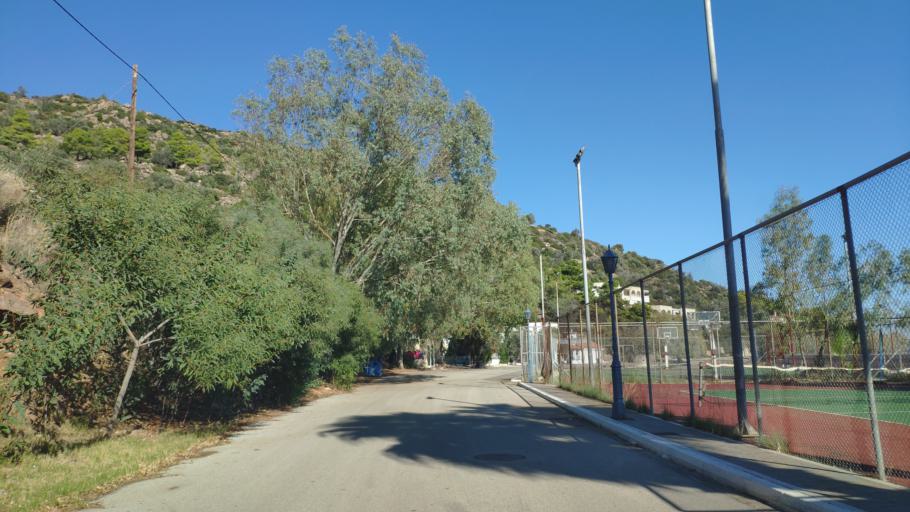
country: GR
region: Attica
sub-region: Nomos Piraios
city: Poros
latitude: 37.5869
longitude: 23.3969
